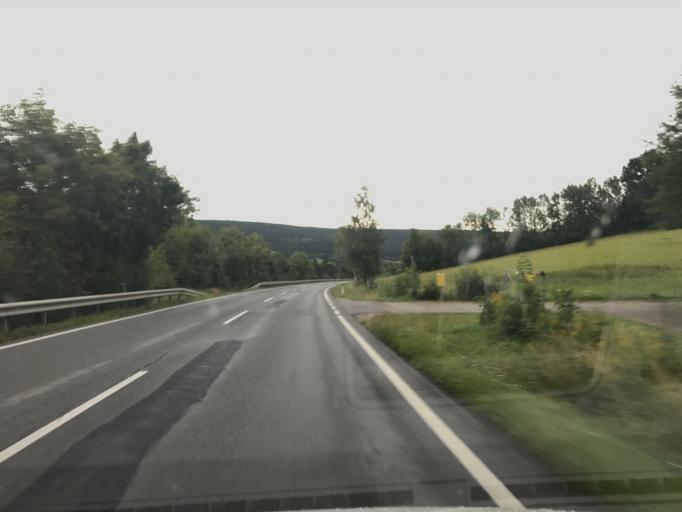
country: AT
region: Lower Austria
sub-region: Politischer Bezirk Wiener Neustadt
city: Markt Piesting
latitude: 47.8692
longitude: 16.1251
